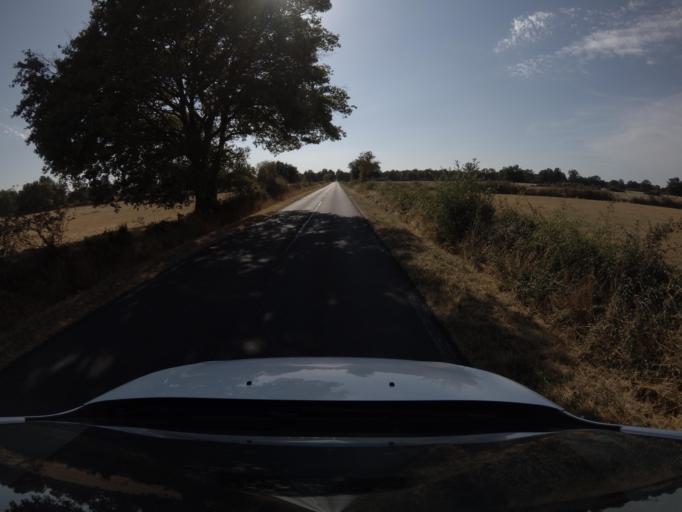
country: FR
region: Poitou-Charentes
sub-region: Departement des Deux-Sevres
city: Argenton-les-Vallees
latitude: 46.9997
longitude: -0.4020
